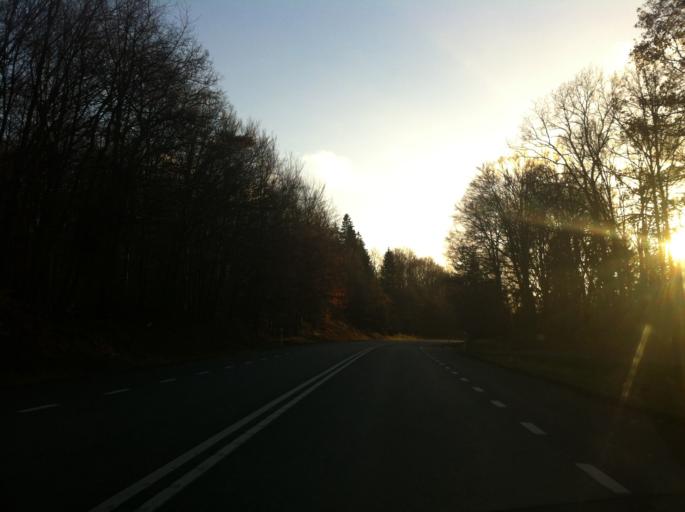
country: SE
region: Skane
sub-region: Hassleholms Kommun
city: Hassleholm
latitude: 56.1480
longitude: 13.8058
